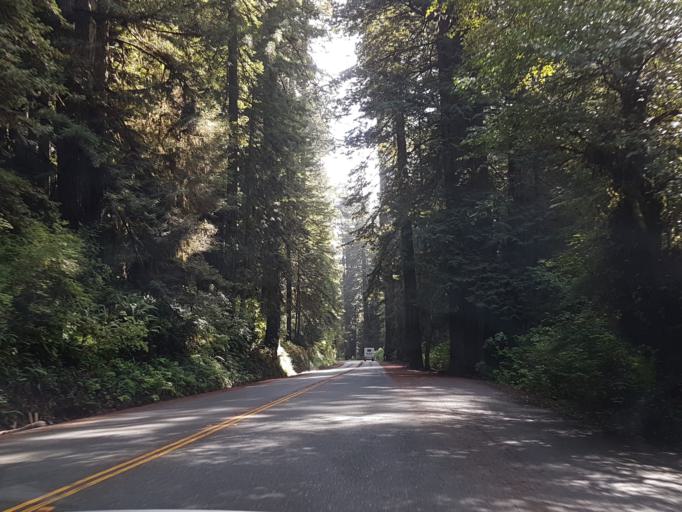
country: US
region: California
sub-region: Del Norte County
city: Bertsch-Oceanview
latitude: 41.4382
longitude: -124.0403
